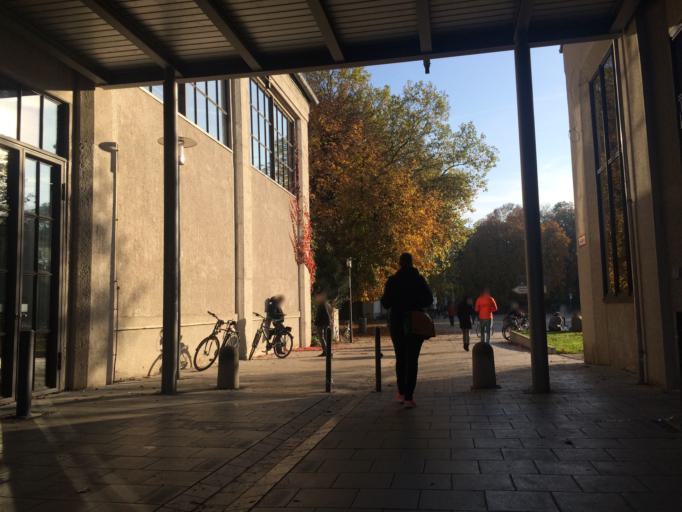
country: DE
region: Bavaria
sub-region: Upper Bavaria
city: Munich
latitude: 48.1330
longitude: 11.5440
